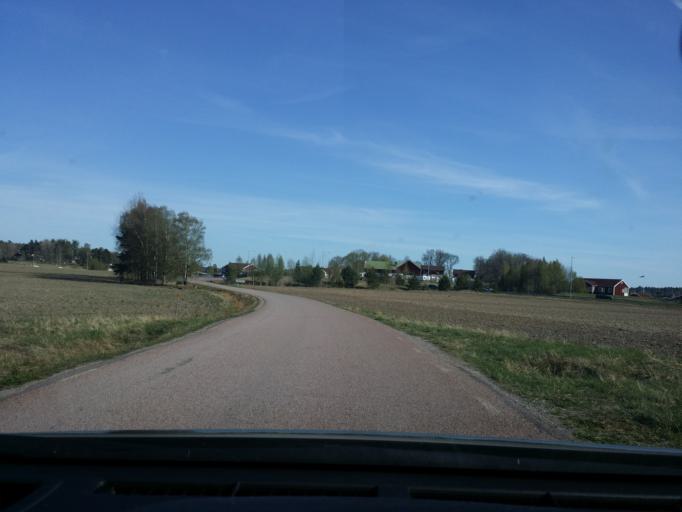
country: SE
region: Vaestmanland
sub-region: Vasteras
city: Vasteras
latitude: 59.6356
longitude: 16.4860
